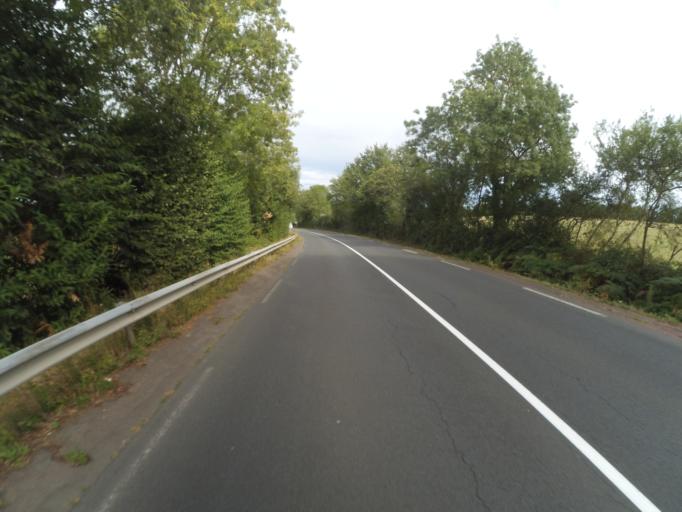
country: FR
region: Poitou-Charentes
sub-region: Departement des Deux-Sevres
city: Saint-Amand-sur-Sevre
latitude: 46.9286
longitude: -0.7807
